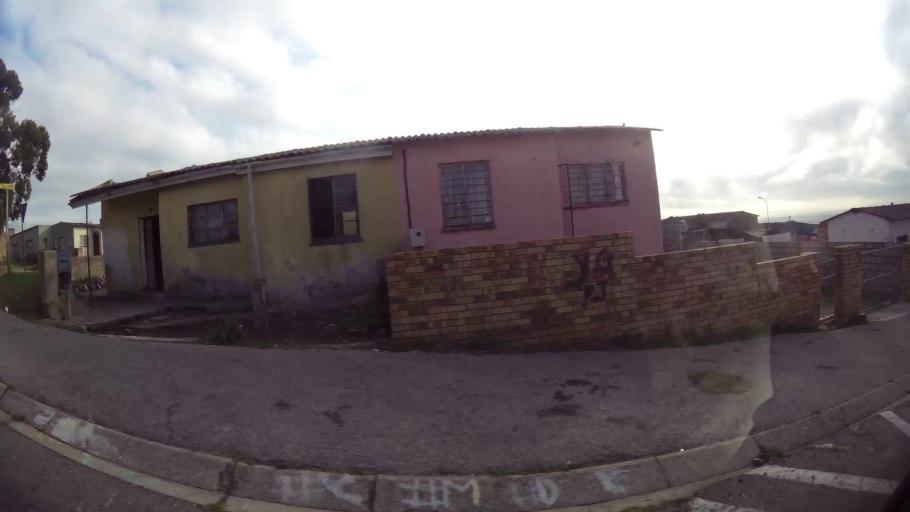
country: ZA
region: Eastern Cape
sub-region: Nelson Mandela Bay Metropolitan Municipality
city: Port Elizabeth
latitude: -33.9195
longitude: 25.5456
